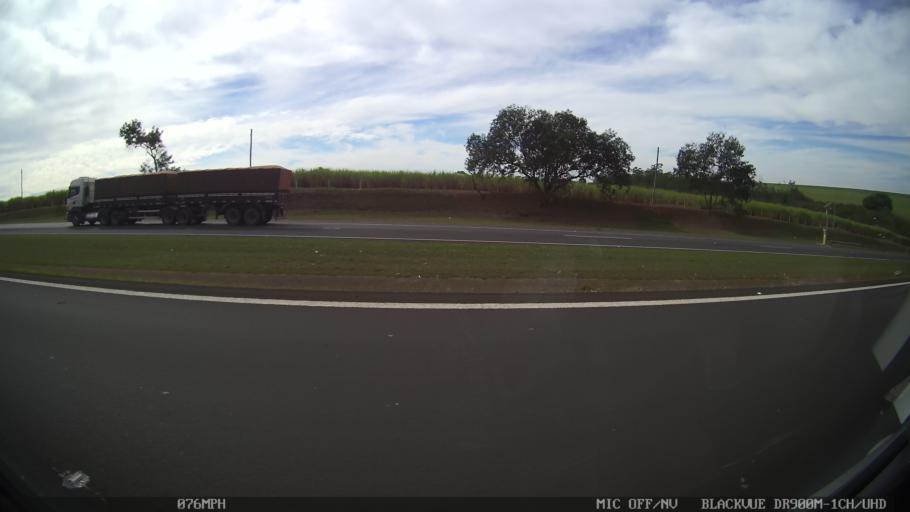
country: BR
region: Sao Paulo
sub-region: Matao
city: Matao
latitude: -21.5515
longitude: -48.4885
